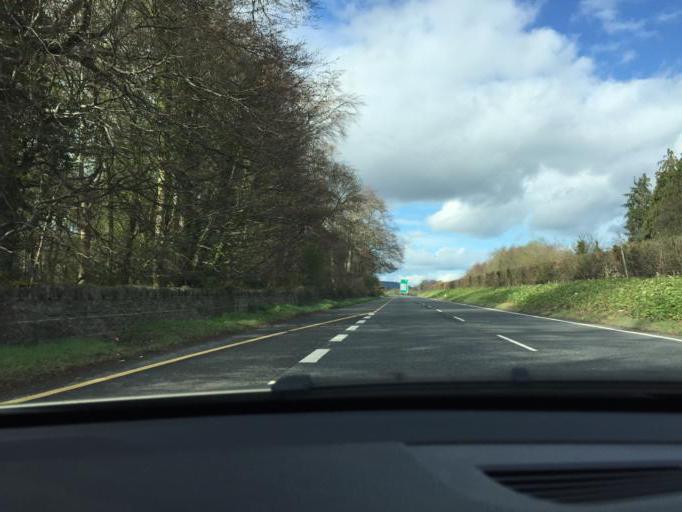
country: IE
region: Leinster
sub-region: Wicklow
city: Kilpedder
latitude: 53.1054
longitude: -6.1073
